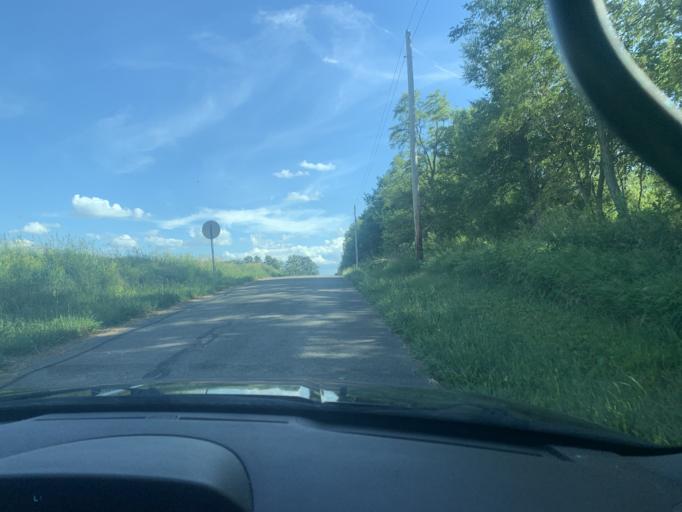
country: US
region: Ohio
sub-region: Logan County
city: De Graff
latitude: 40.3417
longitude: -83.8715
